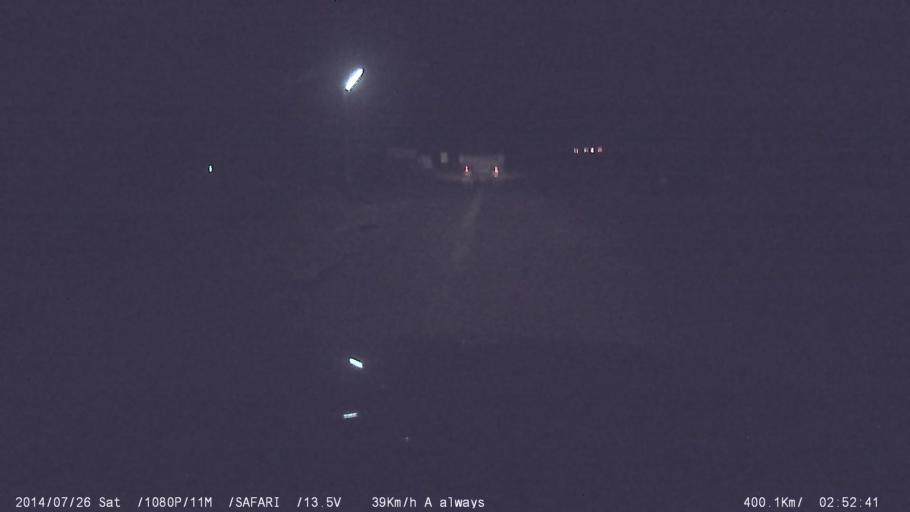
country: IN
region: Kerala
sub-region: Palakkad district
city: Palakkad
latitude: 10.7423
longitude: 76.6577
